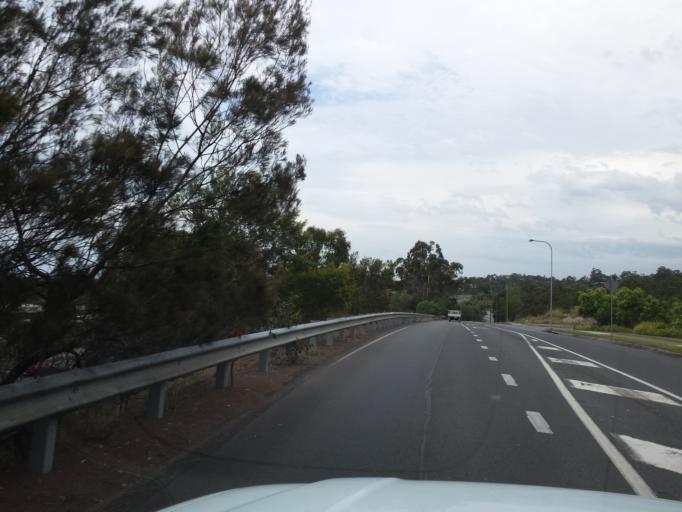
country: AU
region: Queensland
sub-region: Gold Coast
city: Nerang
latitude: -28.0113
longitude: 153.3454
